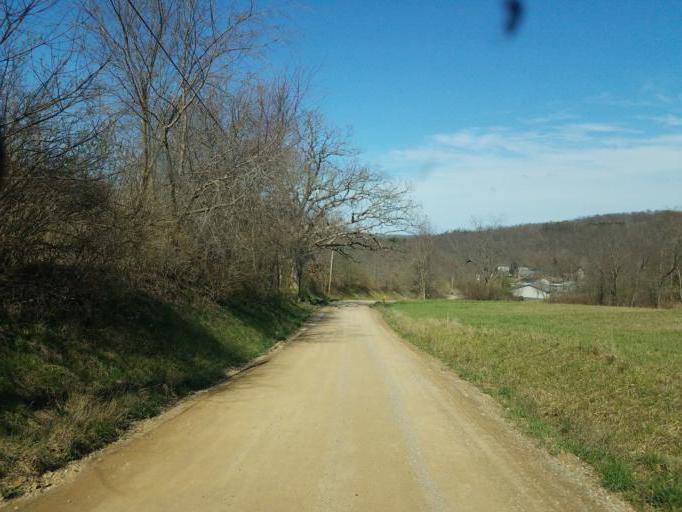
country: US
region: Ohio
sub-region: Knox County
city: Oak Hill
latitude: 40.4013
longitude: -82.2249
